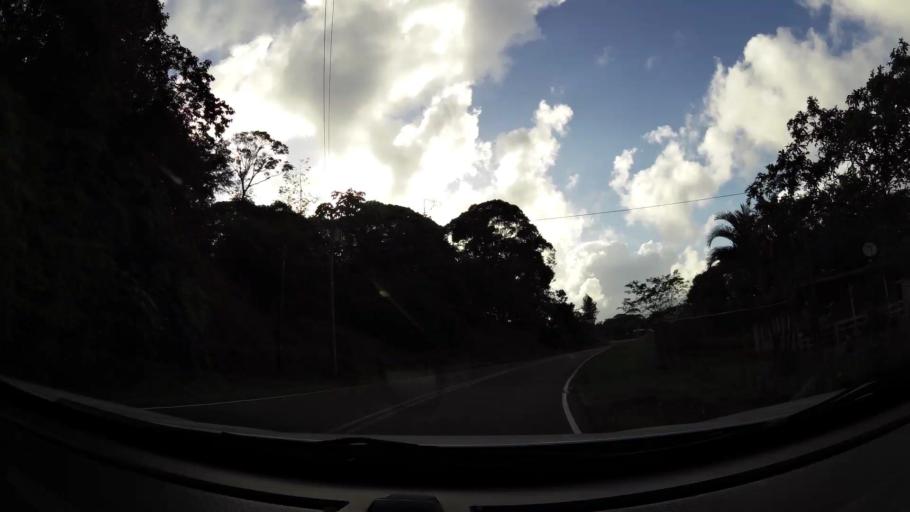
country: CR
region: Limon
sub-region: Canton de Siquirres
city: Siquirres
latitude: 10.0691
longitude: -83.5518
